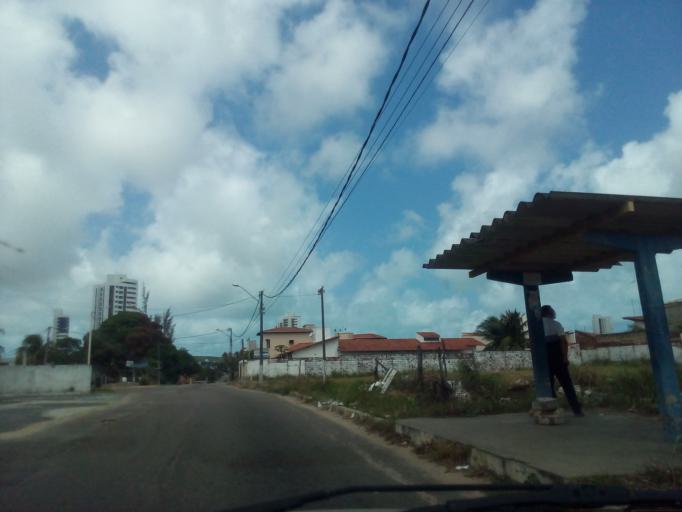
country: BR
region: Rio Grande do Norte
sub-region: Natal
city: Natal
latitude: -5.8599
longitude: -35.2051
